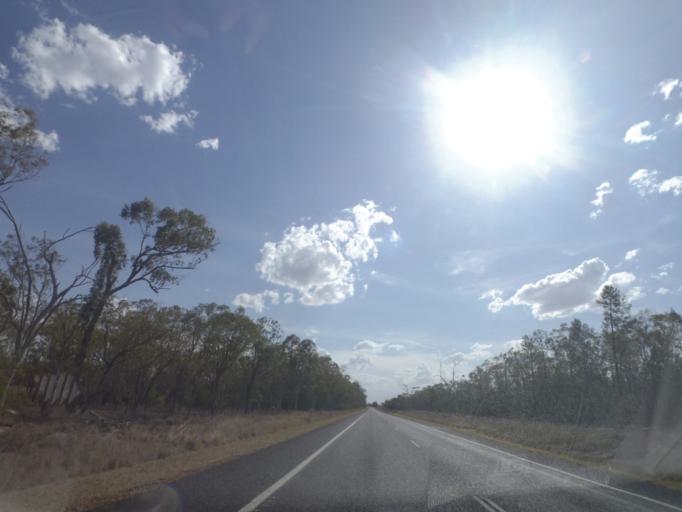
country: AU
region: New South Wales
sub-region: Moree Plains
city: Boggabilla
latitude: -28.5456
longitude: 150.8782
